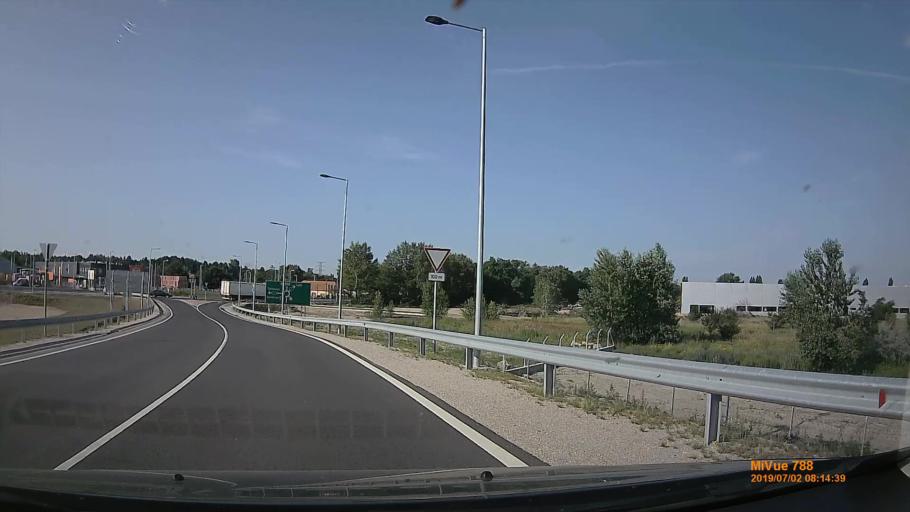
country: HU
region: Komarom-Esztergom
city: Komarom
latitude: 47.7456
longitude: 18.0886
